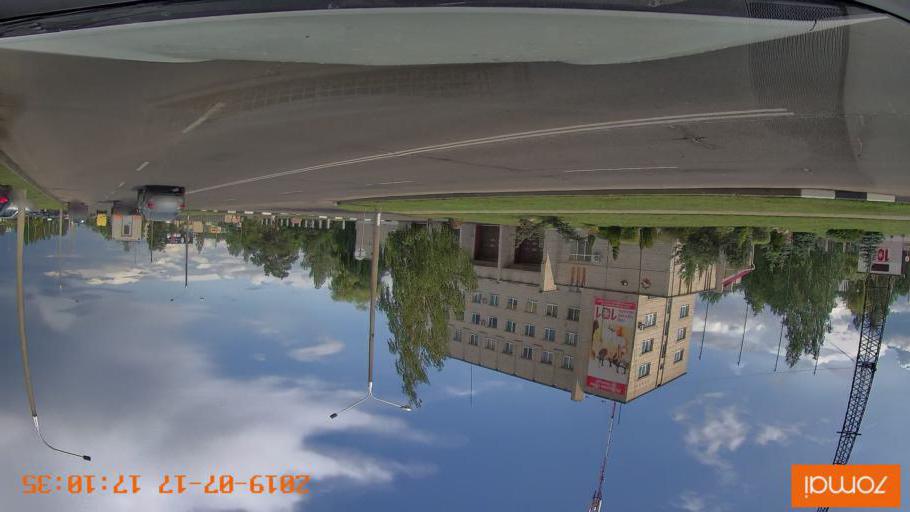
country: BY
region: Mogilev
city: Babruysk
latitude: 53.1696
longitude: 29.1688
